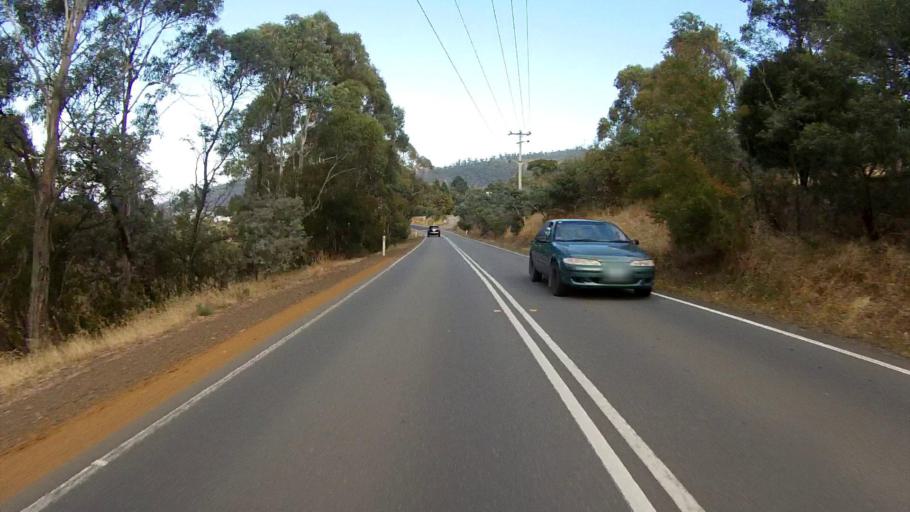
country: AU
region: Tasmania
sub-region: Brighton
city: Bridgewater
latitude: -42.7266
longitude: 147.1906
